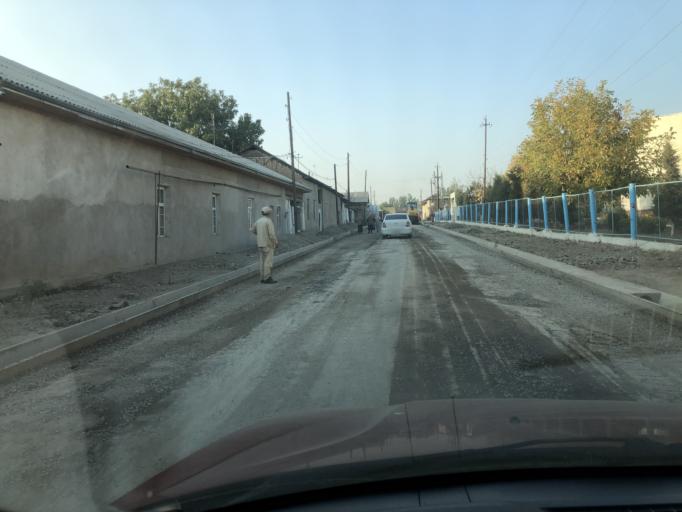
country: UZ
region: Namangan
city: Uychi
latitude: 41.0819
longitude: 71.9996
